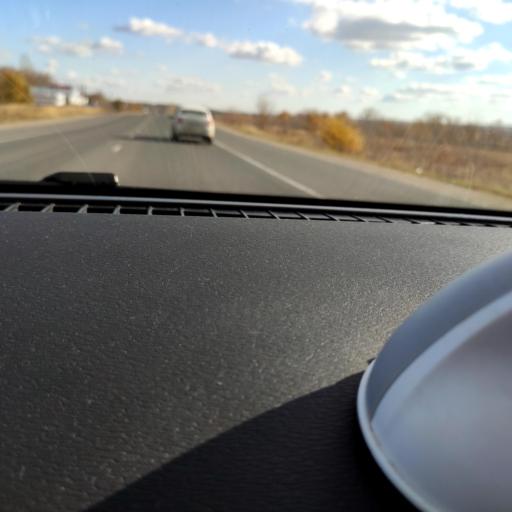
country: RU
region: Samara
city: Samara
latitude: 53.1249
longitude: 50.1812
